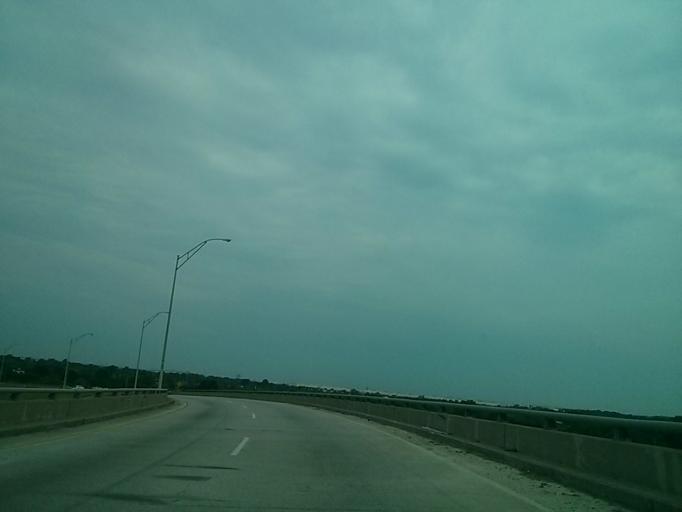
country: US
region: Oklahoma
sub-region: Tulsa County
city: Owasso
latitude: 36.1653
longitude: -95.8605
